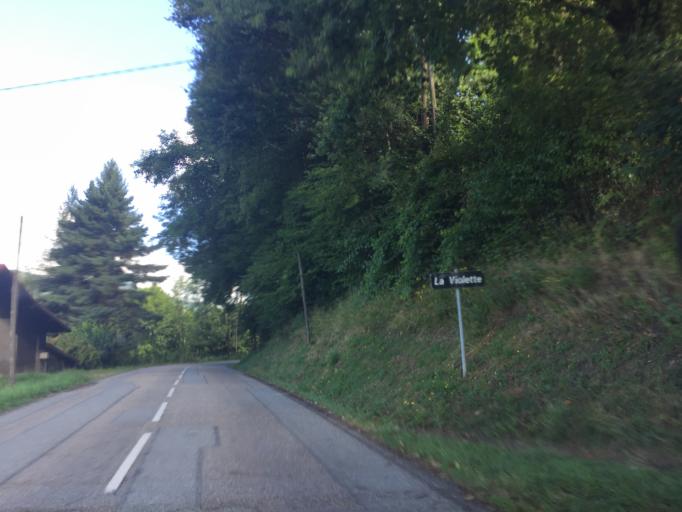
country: FR
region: Rhone-Alpes
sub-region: Departement de la Savoie
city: La Rochette
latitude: 45.4541
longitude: 6.1223
